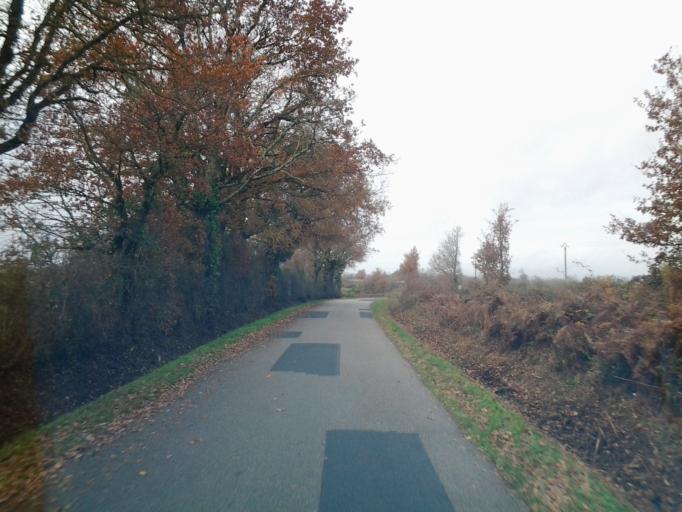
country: FR
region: Pays de la Loire
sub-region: Departement de la Vendee
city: Bournezeau
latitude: 46.6363
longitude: -1.1842
